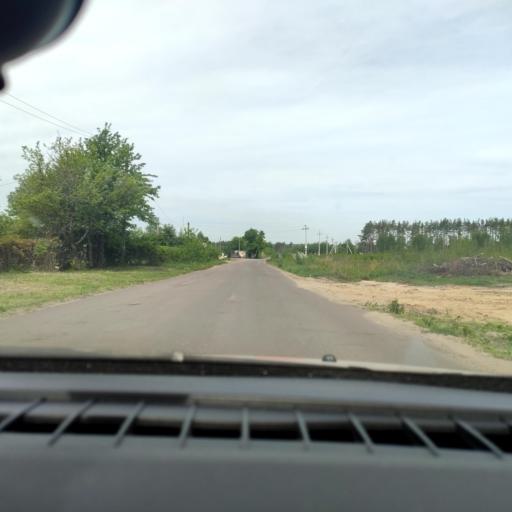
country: RU
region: Voronezj
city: Podgornoye
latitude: 51.8396
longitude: 39.1900
